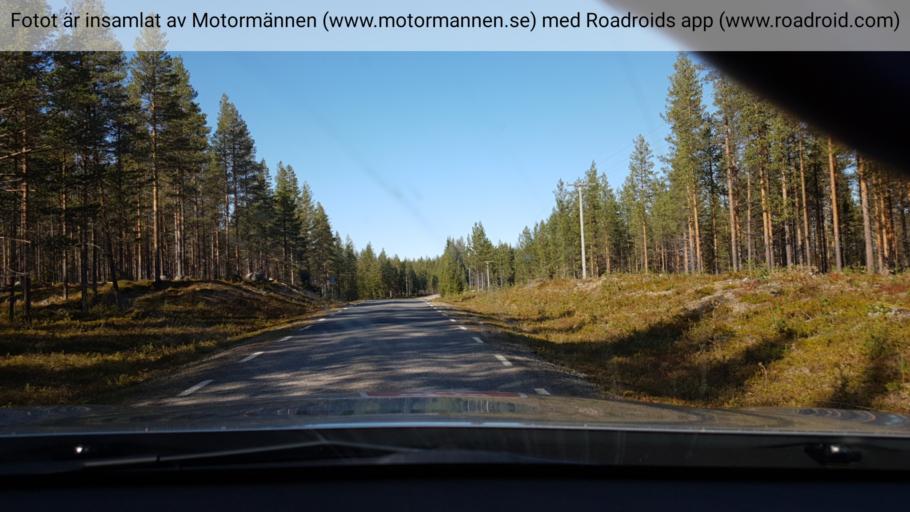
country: SE
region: Vaesterbotten
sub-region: Norsjo Kommun
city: Norsjoe
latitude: 65.1165
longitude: 19.2433
